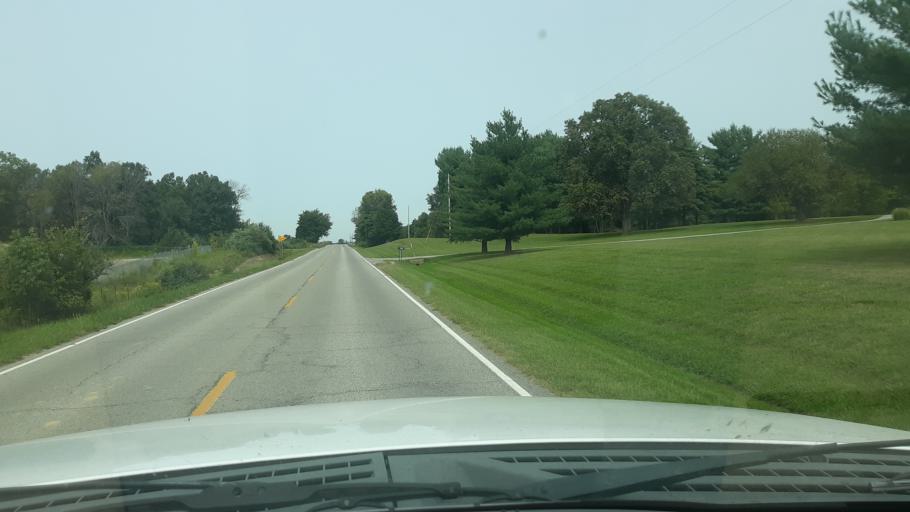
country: US
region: Illinois
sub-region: Saline County
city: Harrisburg
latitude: 37.8595
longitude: -88.6055
